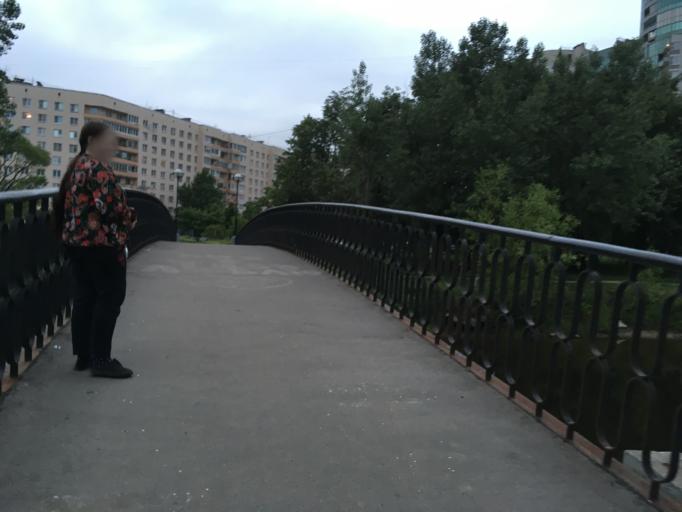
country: RU
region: St.-Petersburg
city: Vasyl'evsky Ostrov
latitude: 59.9466
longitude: 30.2379
